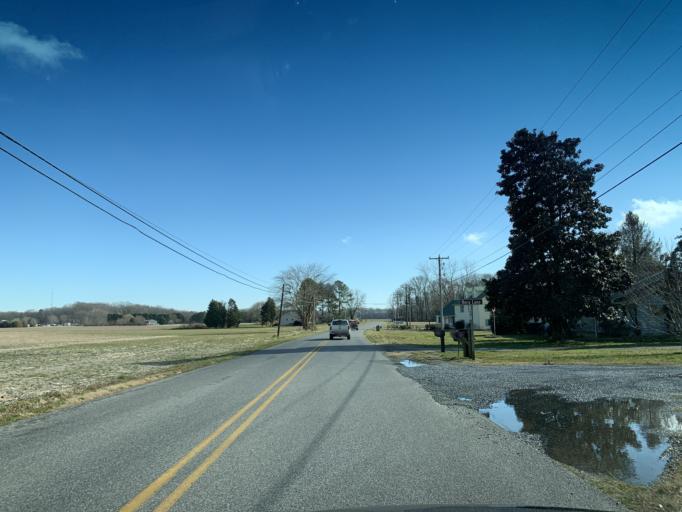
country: US
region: Maryland
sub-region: Worcester County
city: Ocean Pines
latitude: 38.4237
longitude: -75.1660
